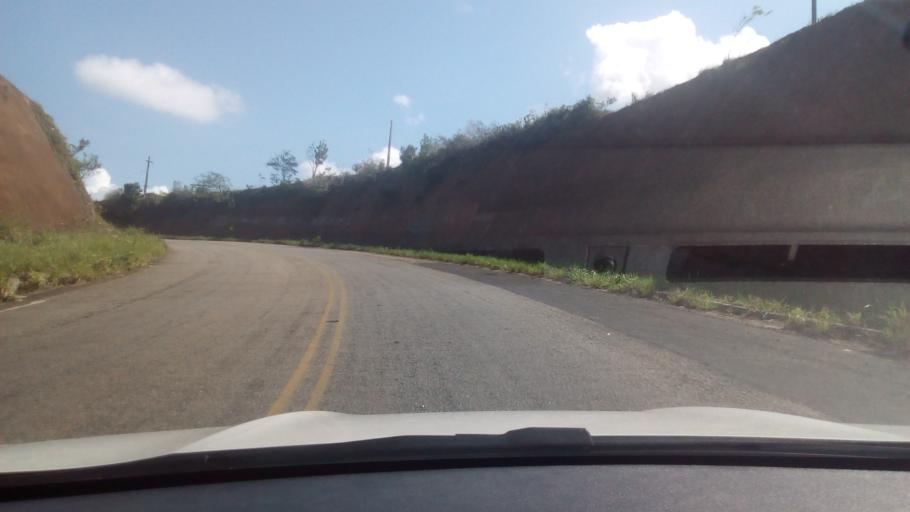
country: BR
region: Paraiba
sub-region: Conde
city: Conde
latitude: -7.2378
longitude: -34.8435
